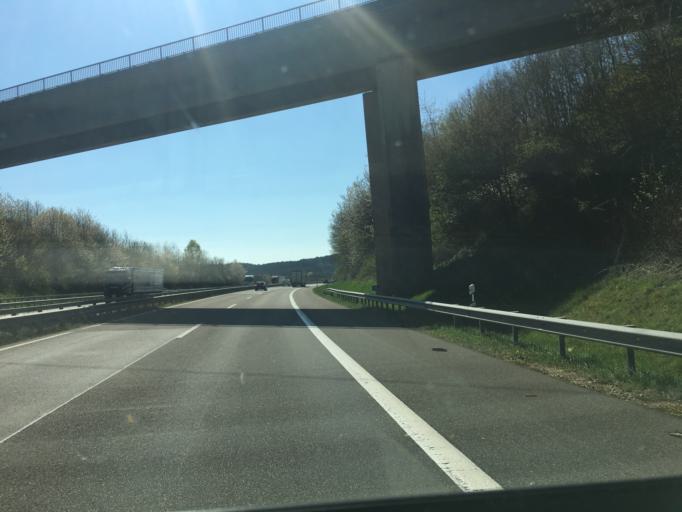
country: DE
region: Rheinland-Pfalz
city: Feuerscheid
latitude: 50.1030
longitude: 6.4438
